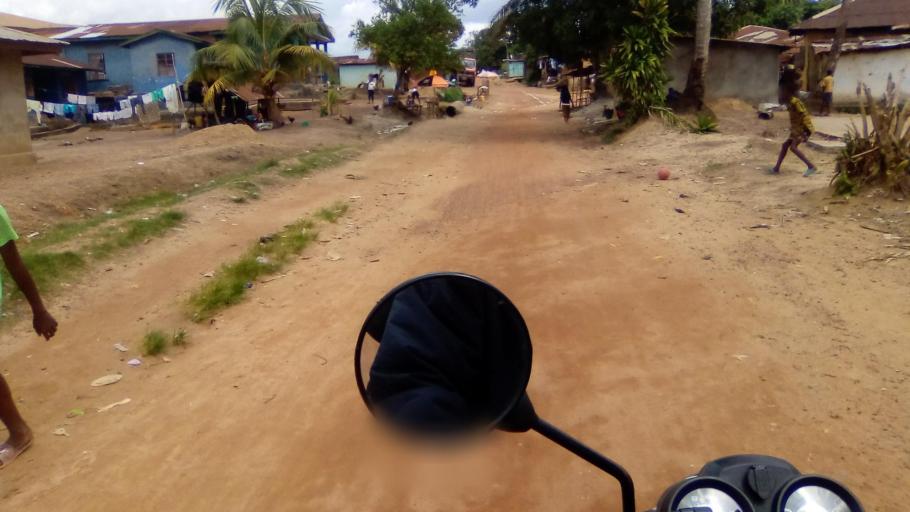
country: SL
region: Southern Province
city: Bo
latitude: 7.9643
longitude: -11.7306
